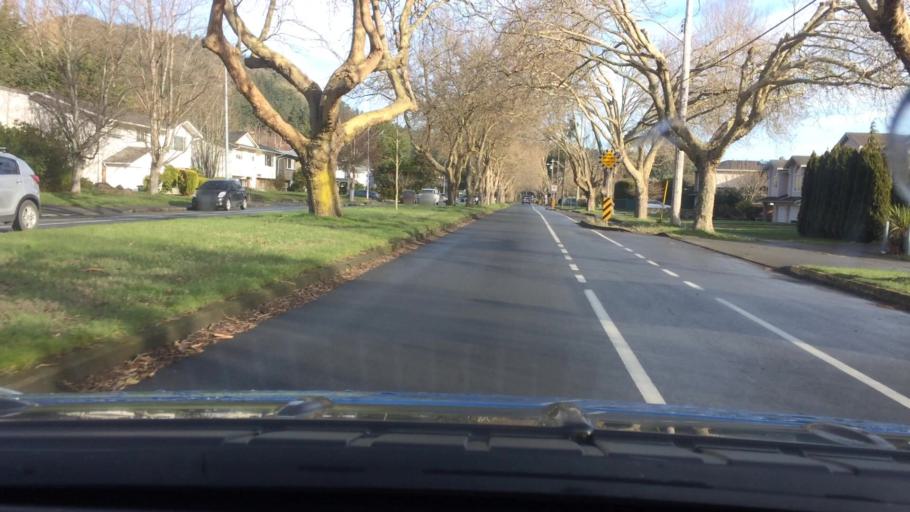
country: CA
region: British Columbia
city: Oak Bay
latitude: 48.4844
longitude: -123.3369
